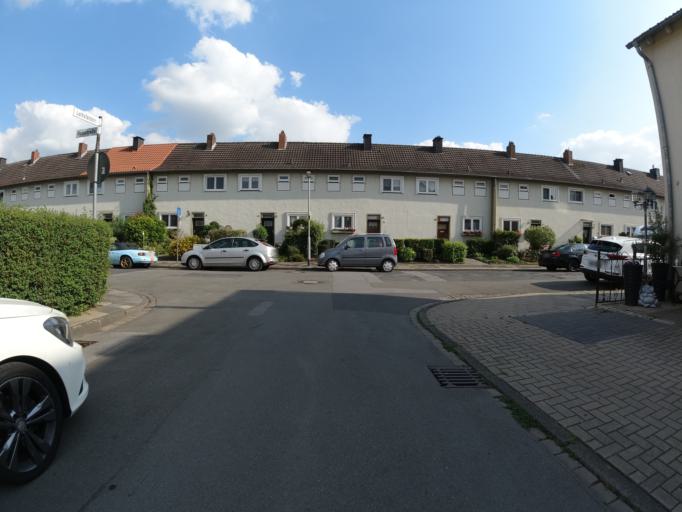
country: DE
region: North Rhine-Westphalia
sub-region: Regierungsbezirk Dusseldorf
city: Hochfeld
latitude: 51.3793
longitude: 6.6886
